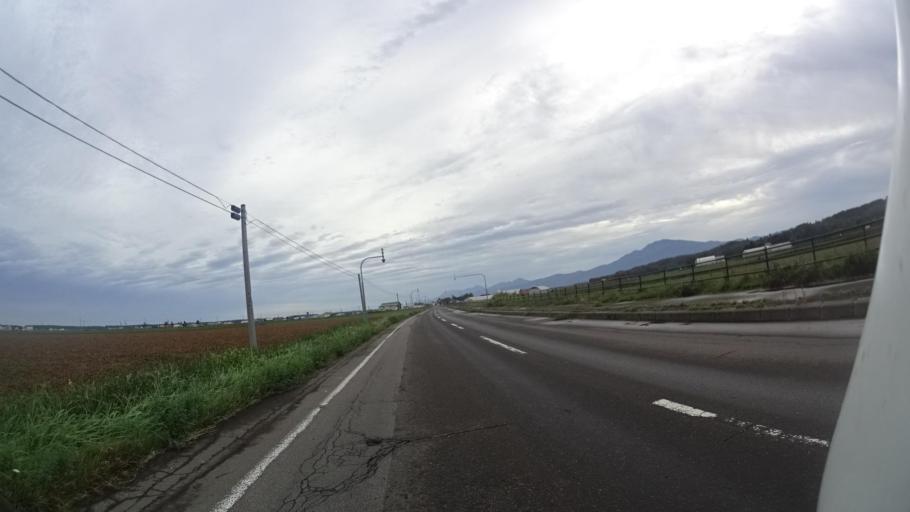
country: JP
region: Hokkaido
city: Abashiri
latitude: 43.8651
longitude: 144.6229
